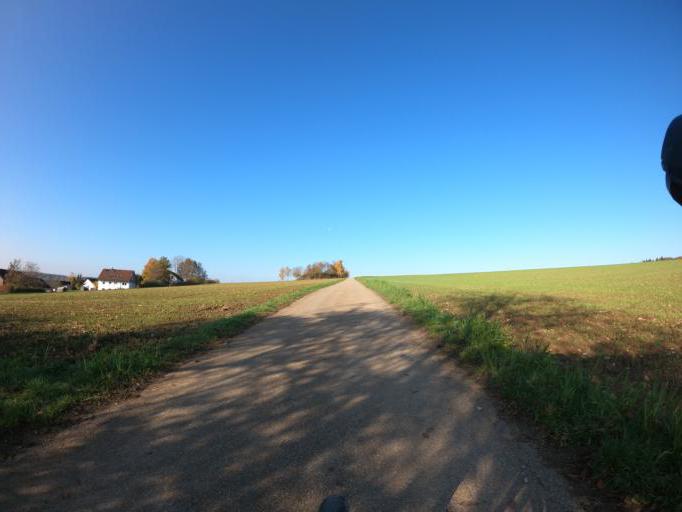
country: DE
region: Baden-Wuerttemberg
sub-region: Regierungsbezirk Stuttgart
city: Aidlingen
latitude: 48.7206
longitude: 8.9102
